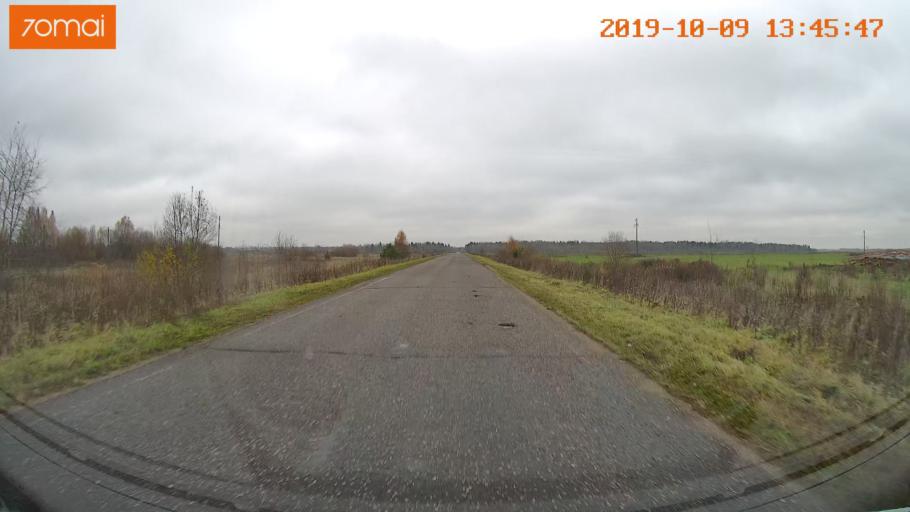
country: RU
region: Kostroma
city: Buy
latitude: 58.3774
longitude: 41.2126
